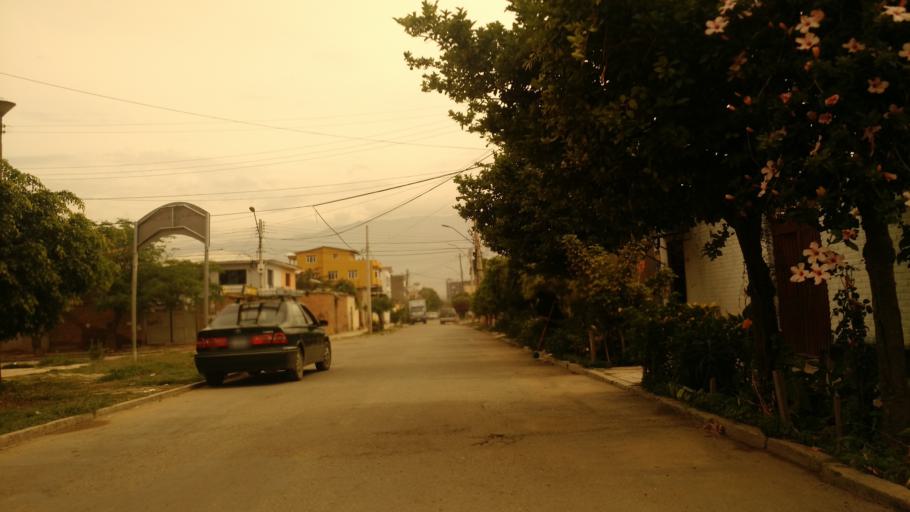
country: BO
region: Cochabamba
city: Cochabamba
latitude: -17.4205
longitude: -66.1559
